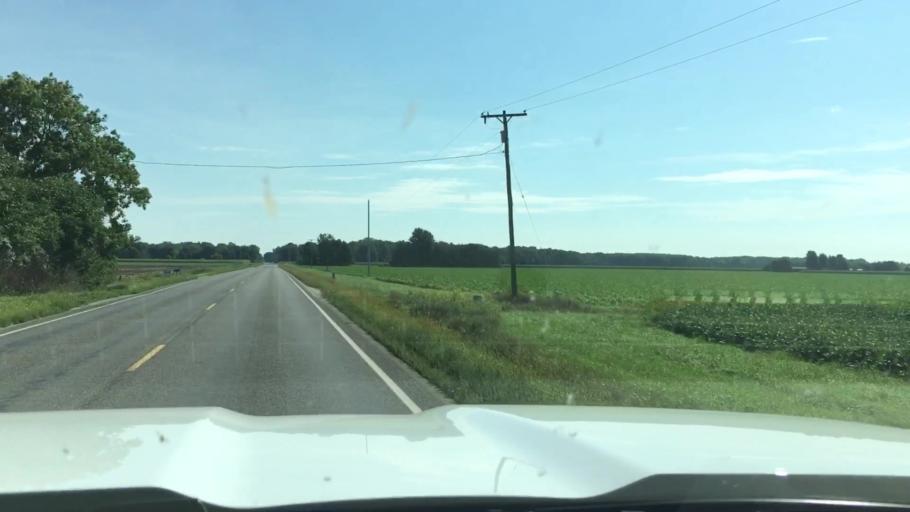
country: US
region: Michigan
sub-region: Saginaw County
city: Freeland
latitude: 43.5253
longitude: -84.1787
